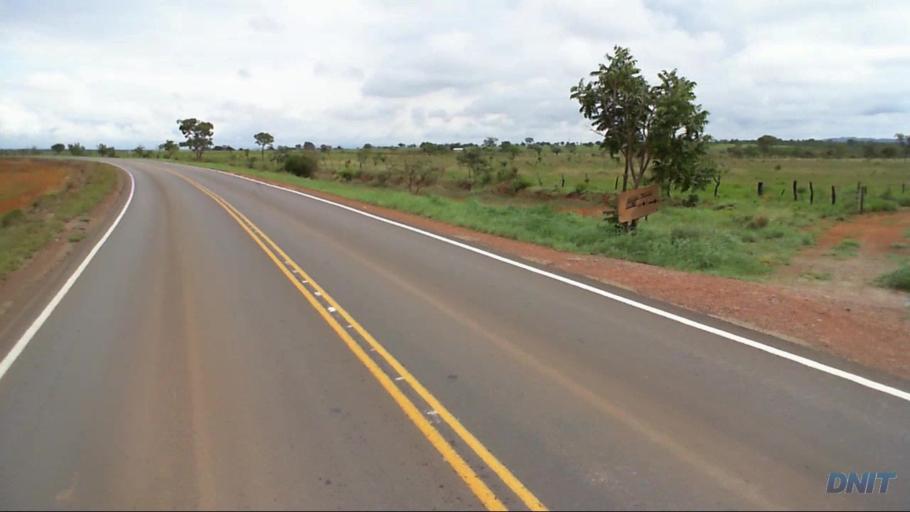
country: BR
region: Goias
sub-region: Padre Bernardo
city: Padre Bernardo
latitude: -15.3064
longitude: -48.2273
